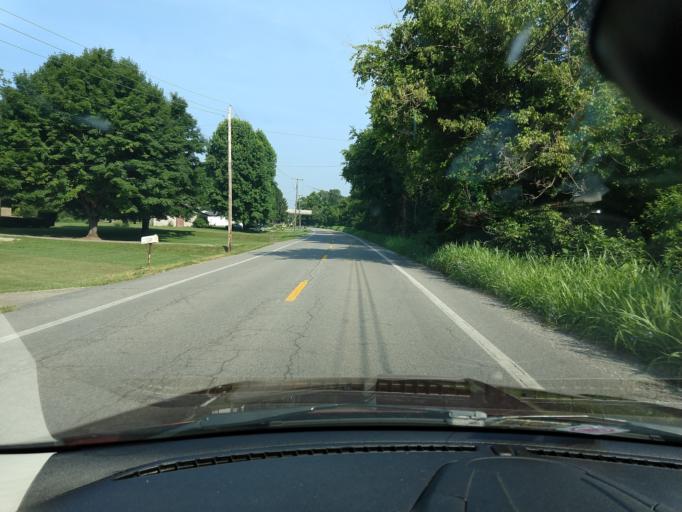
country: US
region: West Virginia
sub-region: Mason County
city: New Haven
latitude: 38.9805
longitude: -81.9460
